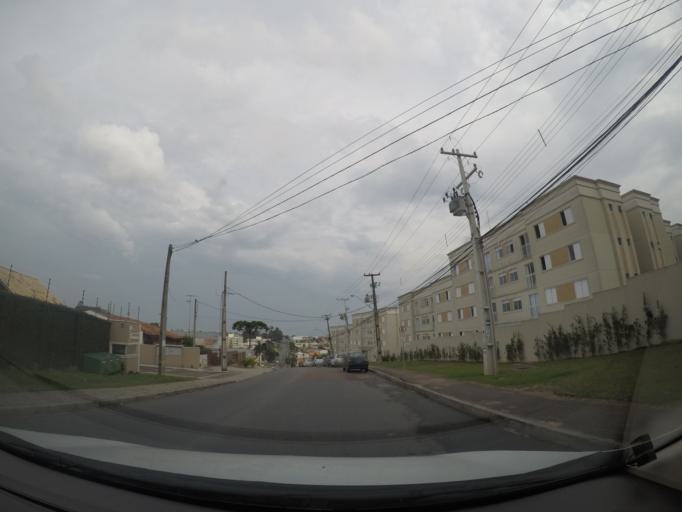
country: BR
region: Parana
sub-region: Sao Jose Dos Pinhais
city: Sao Jose dos Pinhais
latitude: -25.5193
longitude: -49.2615
